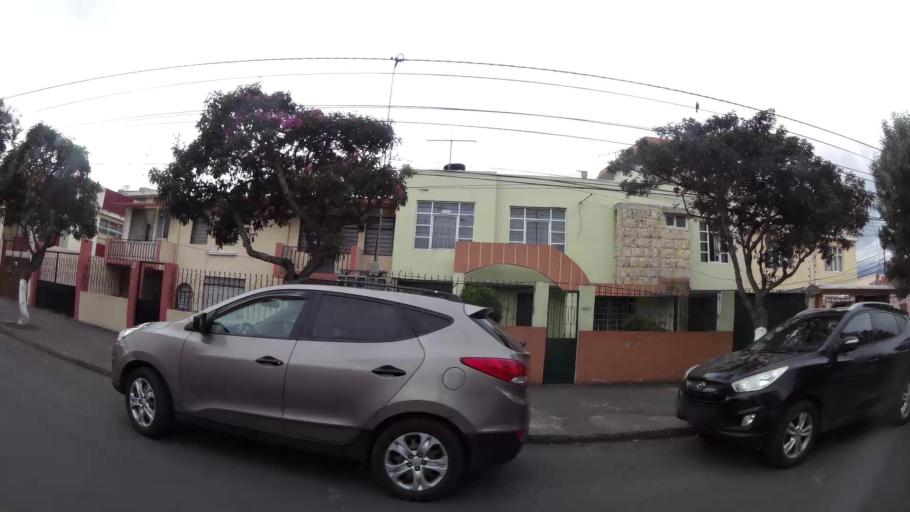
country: EC
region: Tungurahua
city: Ambato
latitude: -1.2524
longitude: -78.6383
